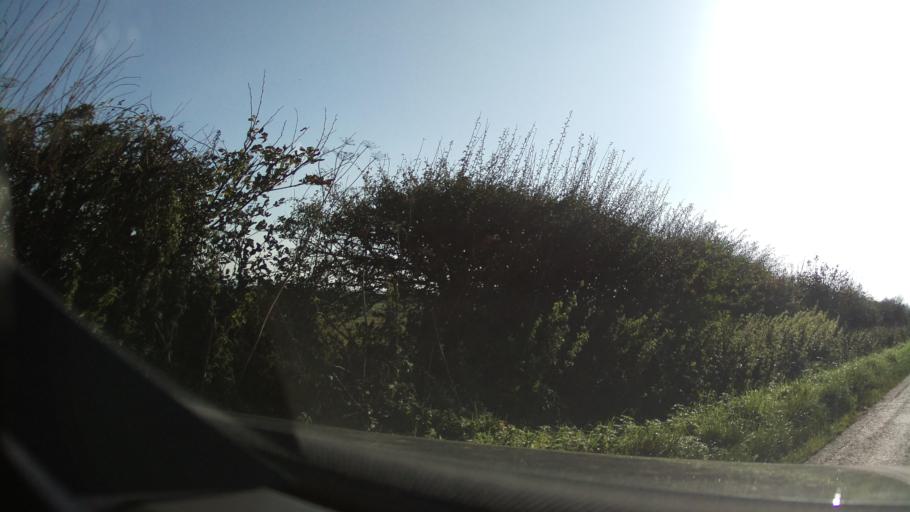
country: GB
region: England
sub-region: Somerset
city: Milborne Port
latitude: 51.0094
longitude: -2.5091
